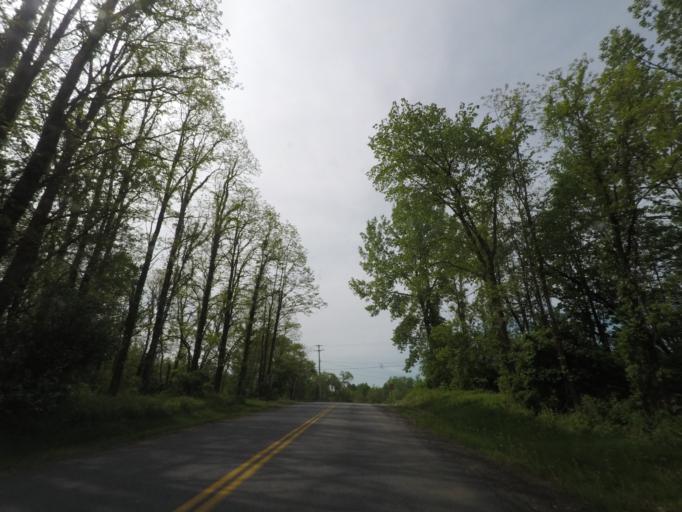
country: US
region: New York
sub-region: Saratoga County
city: Stillwater
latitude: 42.9734
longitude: -73.7147
